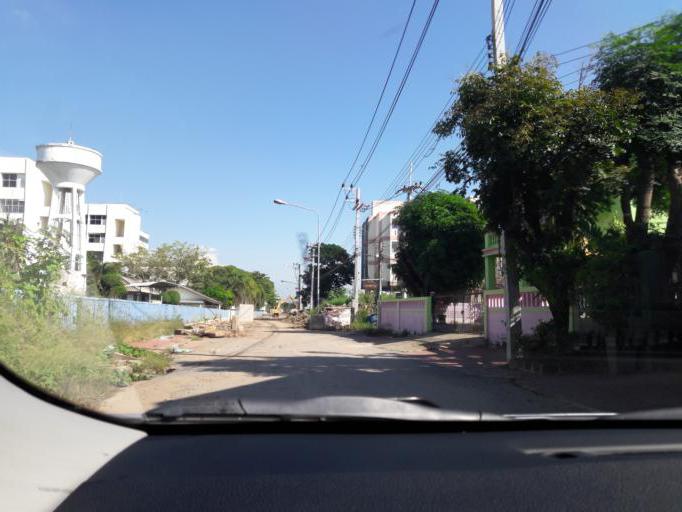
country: TH
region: Ang Thong
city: Ang Thong
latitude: 14.5856
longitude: 100.4497
